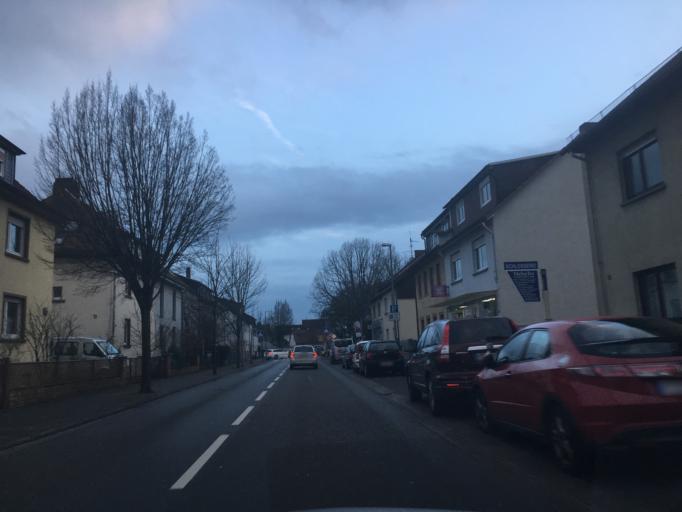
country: DE
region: Hesse
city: Kelsterbach
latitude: 50.0548
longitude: 8.4989
